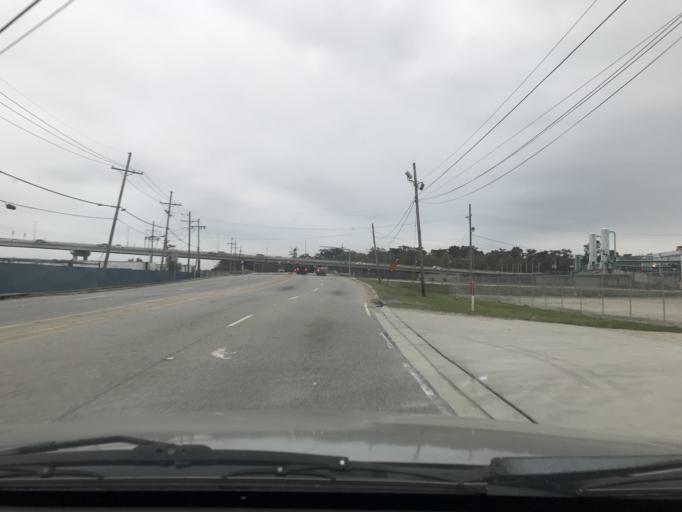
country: US
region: Louisiana
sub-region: Jefferson Parish
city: Woodmere
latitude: 29.8727
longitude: -90.0728
